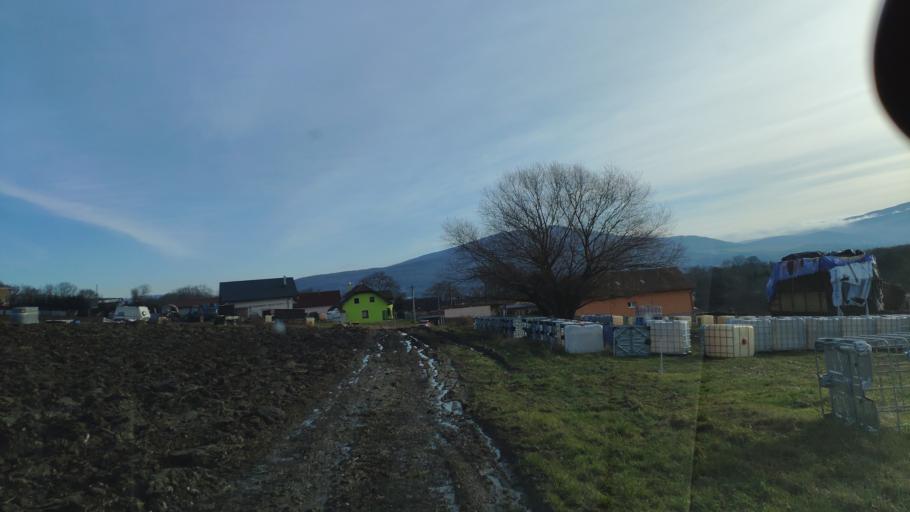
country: SK
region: Kosicky
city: Kosice
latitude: 48.6866
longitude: 21.3931
